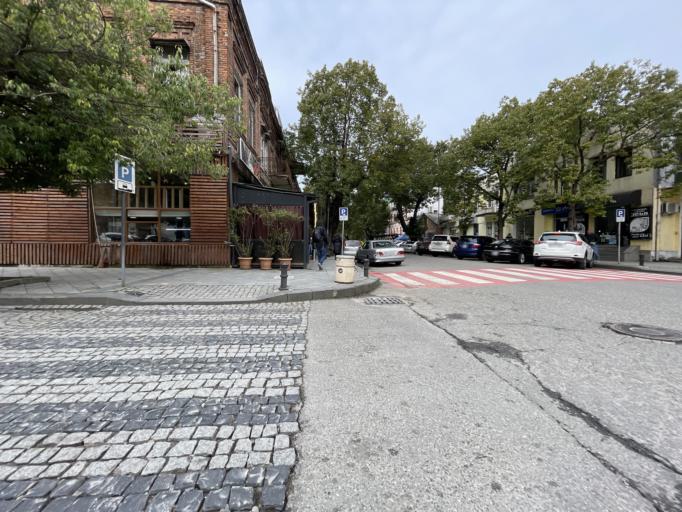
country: GE
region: Ajaria
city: Batumi
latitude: 41.6486
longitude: 41.6397
